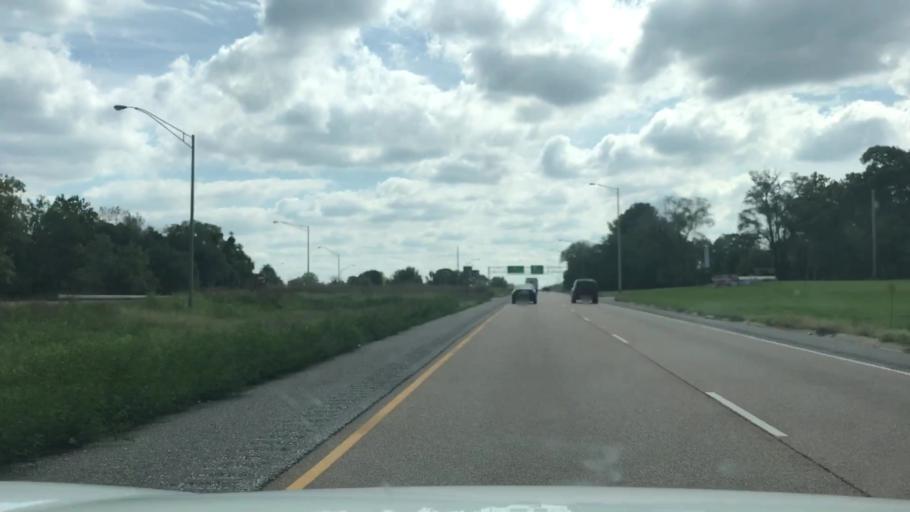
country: US
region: Illinois
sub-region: Saint Clair County
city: Alorton
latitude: 38.5505
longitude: -90.0708
